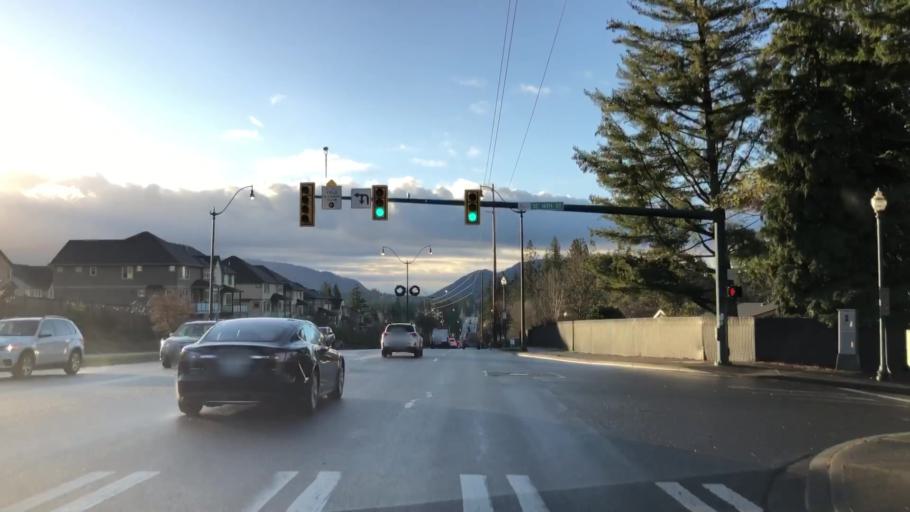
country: US
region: Washington
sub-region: King County
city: City of Sammamish
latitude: 47.5956
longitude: -122.0356
